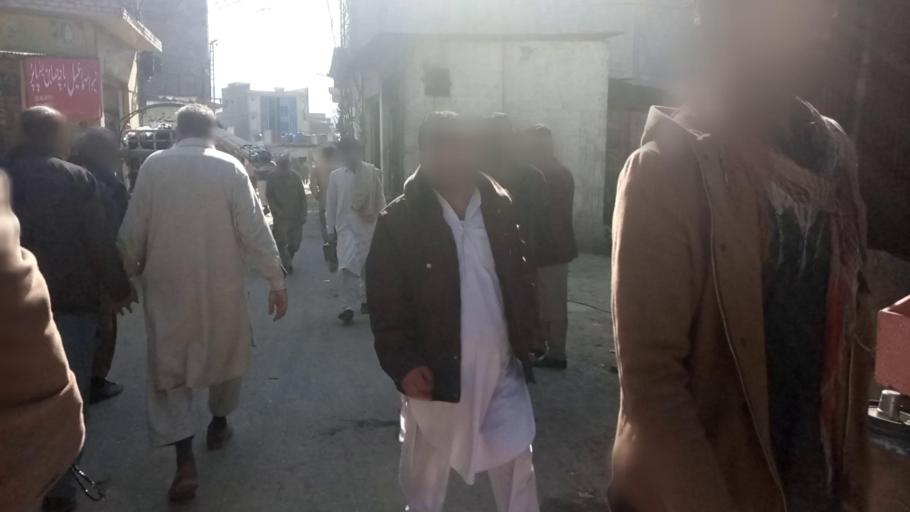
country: PK
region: Khyber Pakhtunkhwa
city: Mingora
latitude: 34.7803
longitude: 72.3595
